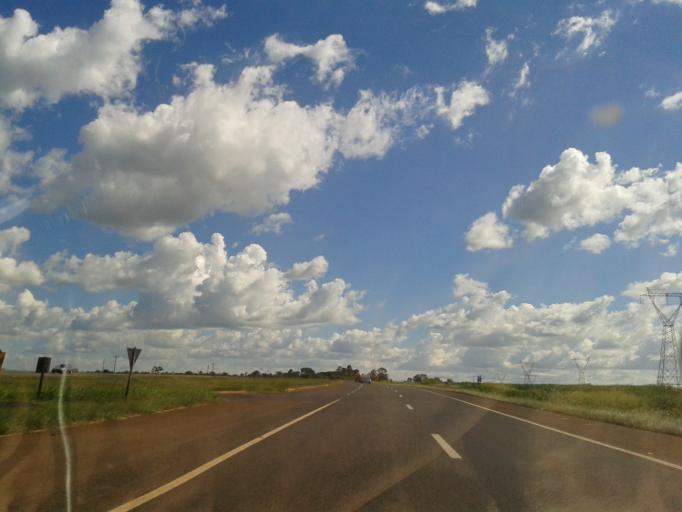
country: BR
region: Goias
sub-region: Goiatuba
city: Goiatuba
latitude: -17.8927
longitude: -49.2341
